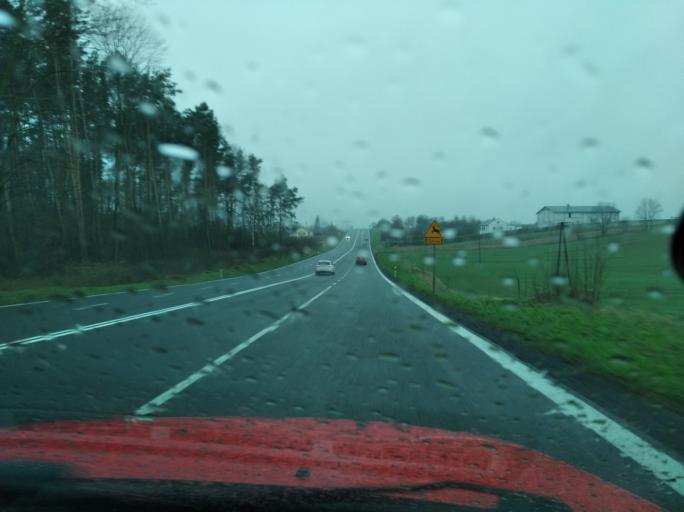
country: PL
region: Subcarpathian Voivodeship
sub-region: Powiat przeworski
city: Nowosielce
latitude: 50.0647
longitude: 22.4228
